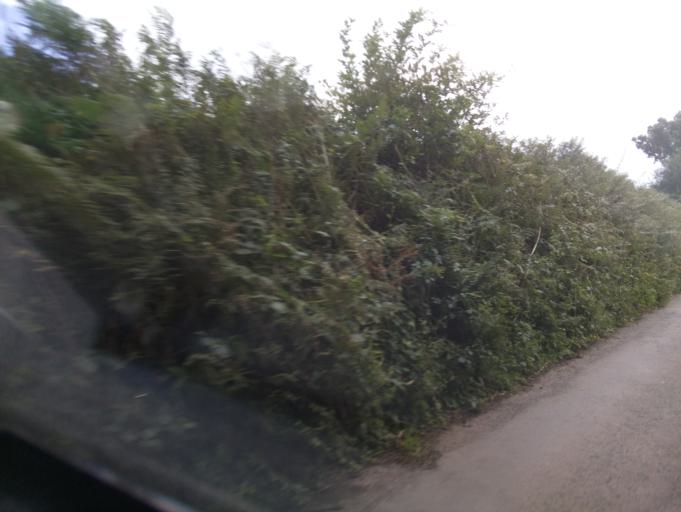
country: GB
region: England
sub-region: Devon
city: Totnes
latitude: 50.3993
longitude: -3.7114
